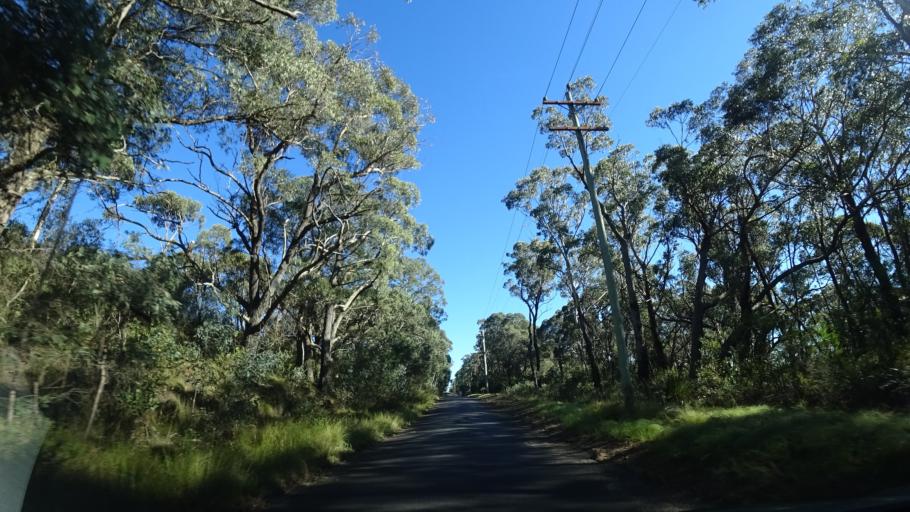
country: AU
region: New South Wales
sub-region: Blue Mountains Municipality
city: Blackheath
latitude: -33.5083
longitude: 150.2809
